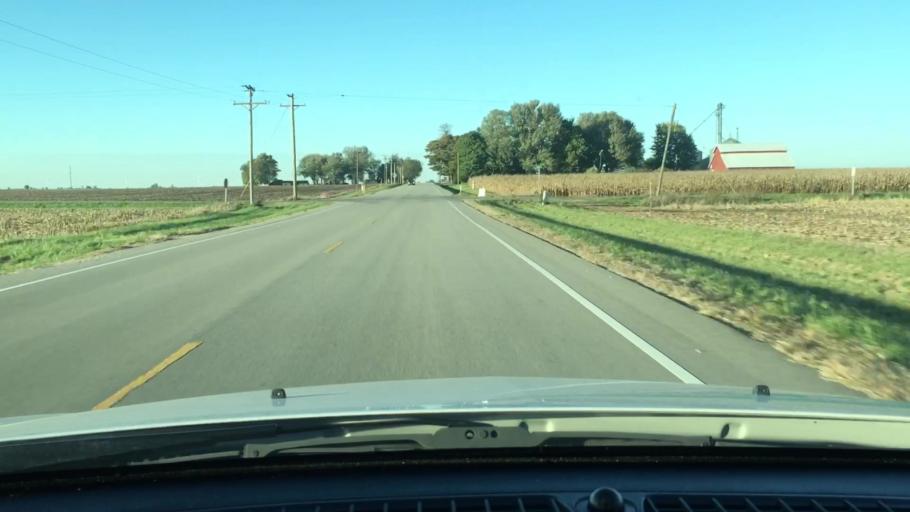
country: US
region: Illinois
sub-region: DeKalb County
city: Malta
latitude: 41.8188
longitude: -88.8864
